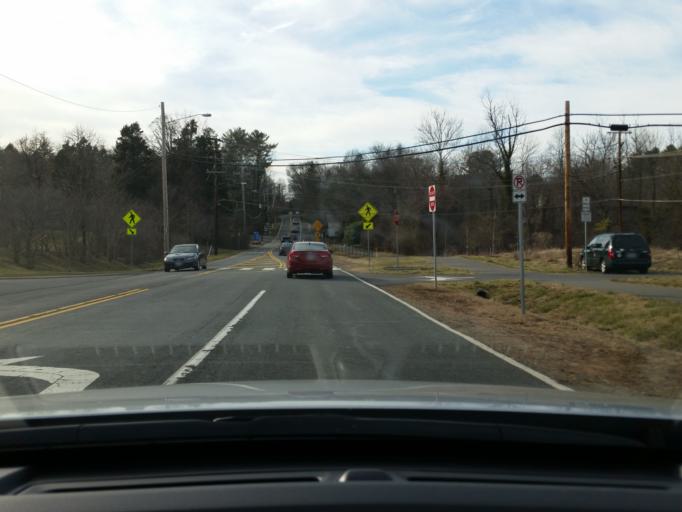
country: US
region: Virginia
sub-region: Fairfax County
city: McLean
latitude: 38.9458
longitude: -77.1556
